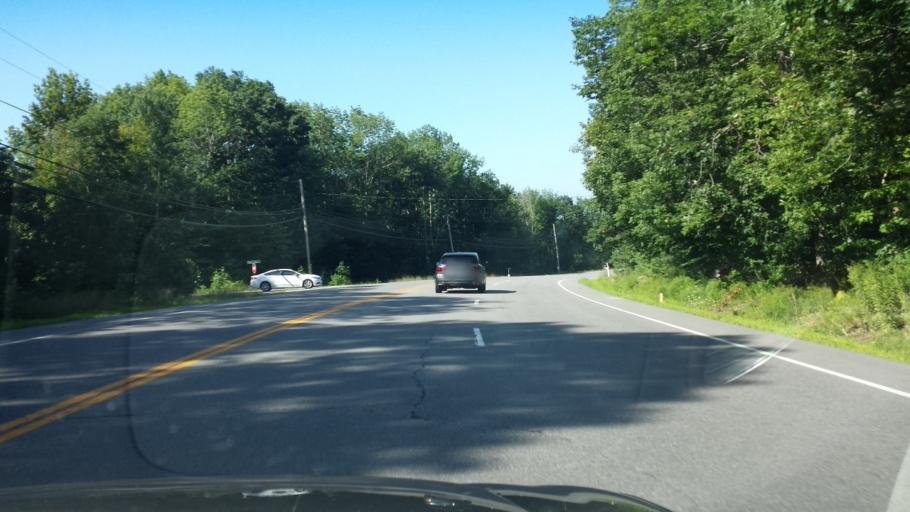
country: US
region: Maine
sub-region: York County
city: Sanford (historical)
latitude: 43.4228
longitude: -70.8159
